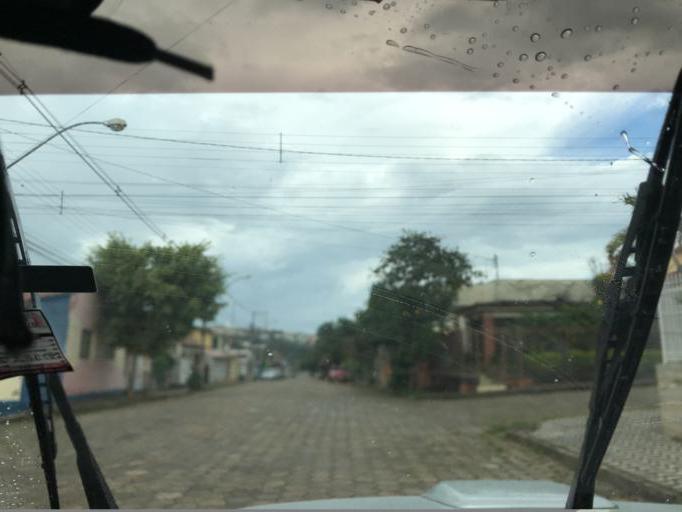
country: BR
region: Minas Gerais
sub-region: Tres Coracoes
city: Tres Coracoes
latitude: -21.7051
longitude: -45.2519
